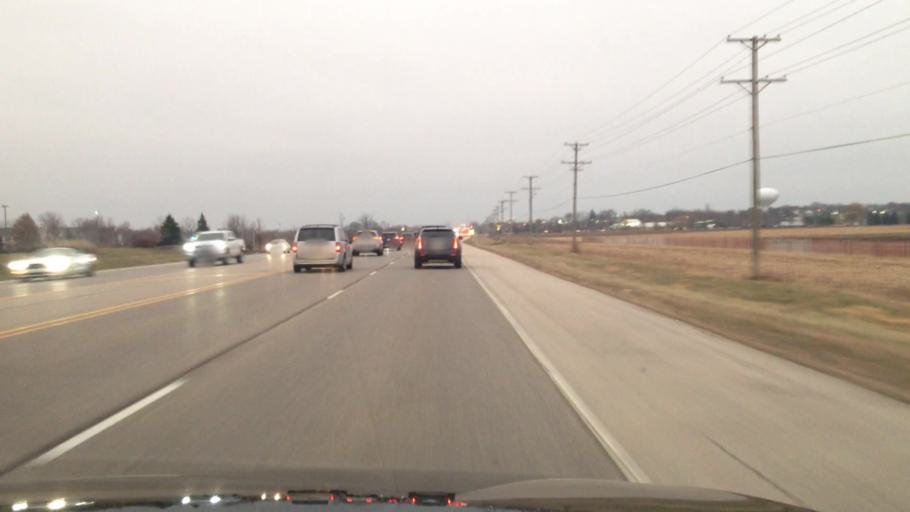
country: US
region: Illinois
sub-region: McHenry County
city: Lake in the Hills
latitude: 42.1344
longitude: -88.3357
